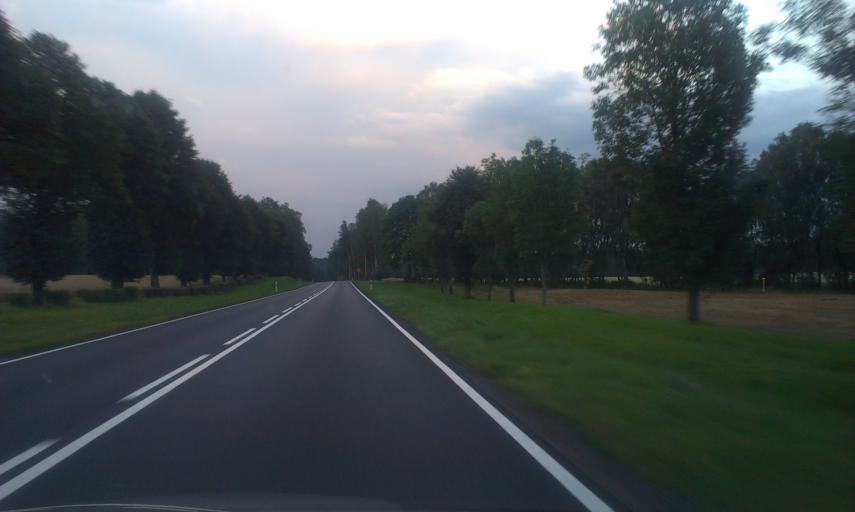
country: PL
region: West Pomeranian Voivodeship
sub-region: Powiat koszalinski
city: Bobolice
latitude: 54.0164
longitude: 16.4919
